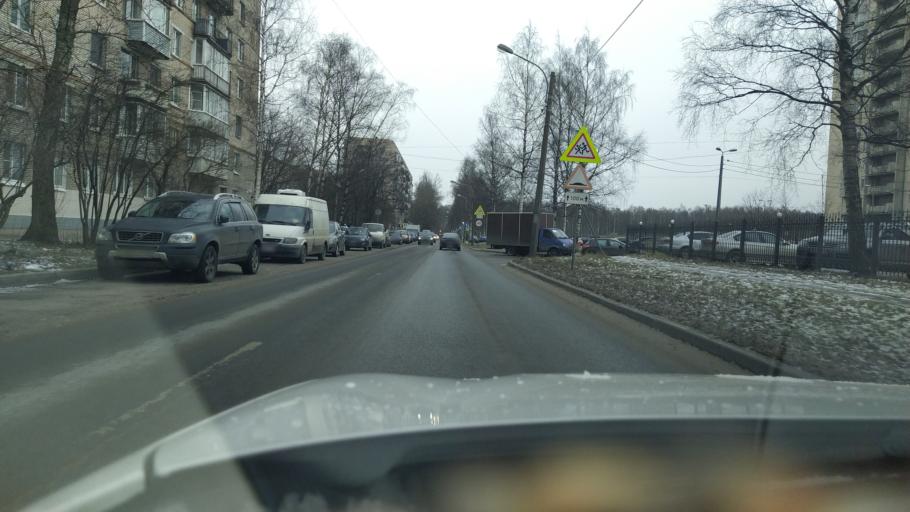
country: RU
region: Leningrad
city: Kalininskiy
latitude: 60.0011
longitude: 30.3893
